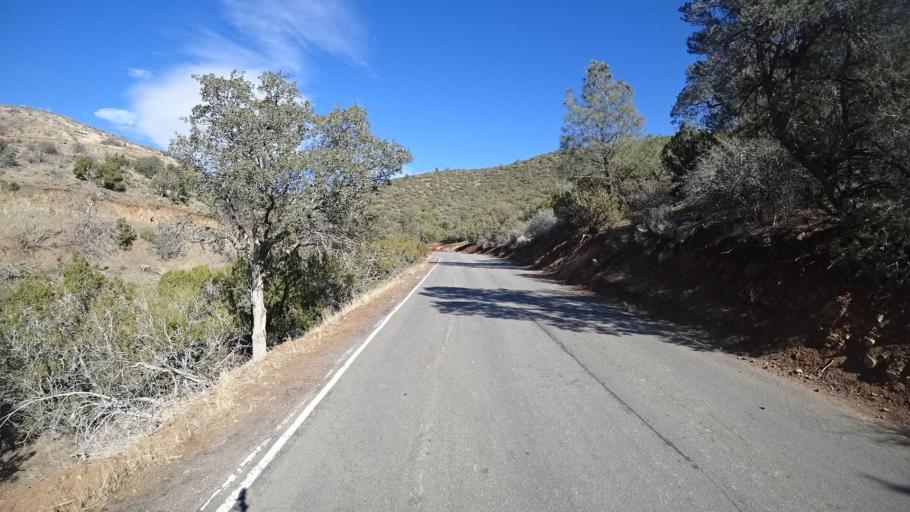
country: US
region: California
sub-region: Kern County
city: Bodfish
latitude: 35.5653
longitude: -118.5033
